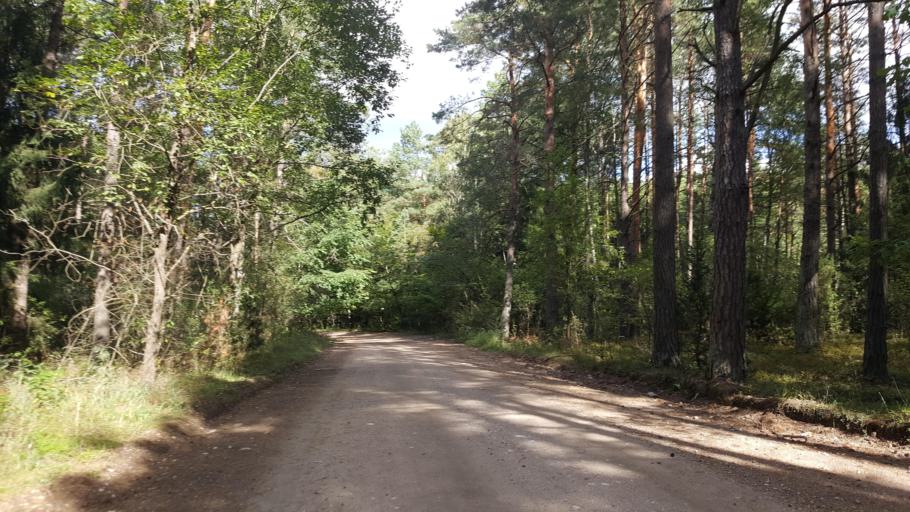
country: BY
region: Brest
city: Kamyanyets
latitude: 52.4284
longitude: 23.9433
